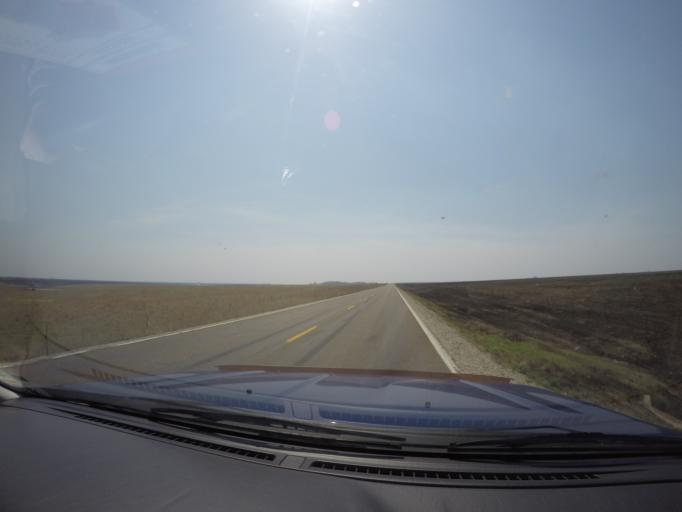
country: US
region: Kansas
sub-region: Morris County
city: Council Grove
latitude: 38.5268
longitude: -96.5287
